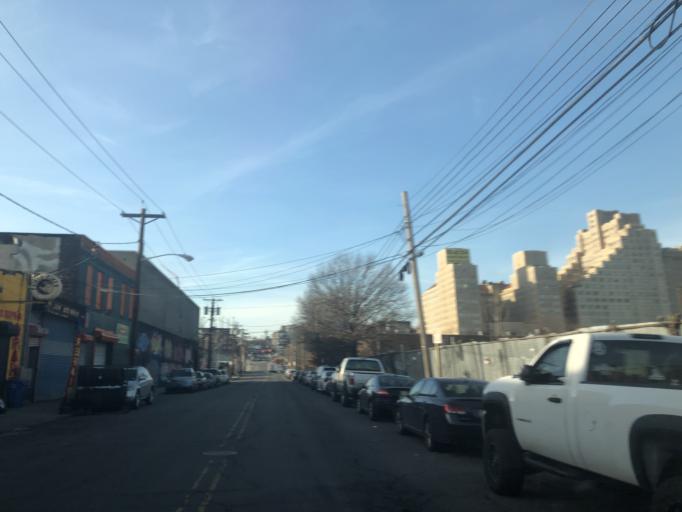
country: US
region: New Jersey
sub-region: Hudson County
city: Jersey City
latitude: 40.7180
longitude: -74.0624
